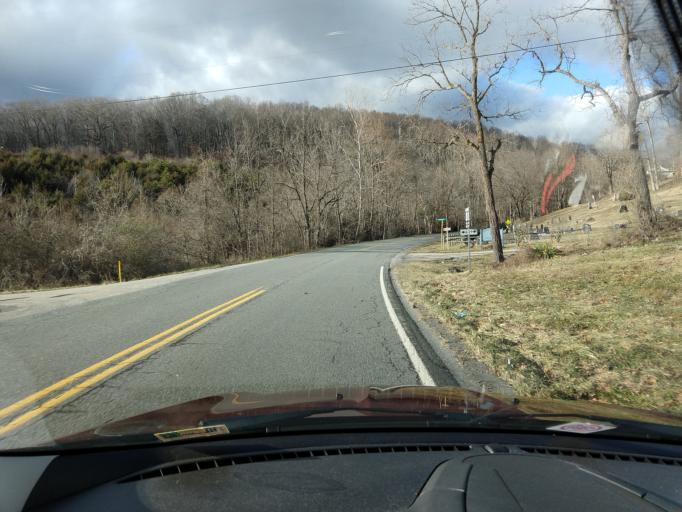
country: US
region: Virginia
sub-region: City of Lexington
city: Lexington
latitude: 37.8222
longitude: -79.4954
